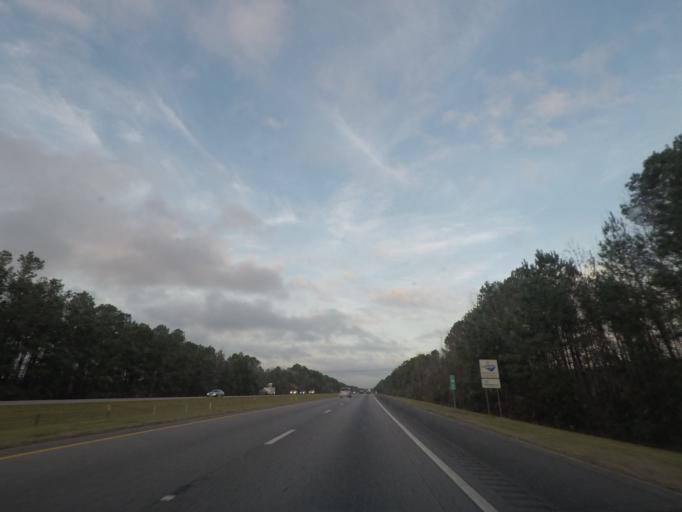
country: US
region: South Carolina
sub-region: Orangeburg County
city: Holly Hill
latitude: 33.4026
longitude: -80.5087
